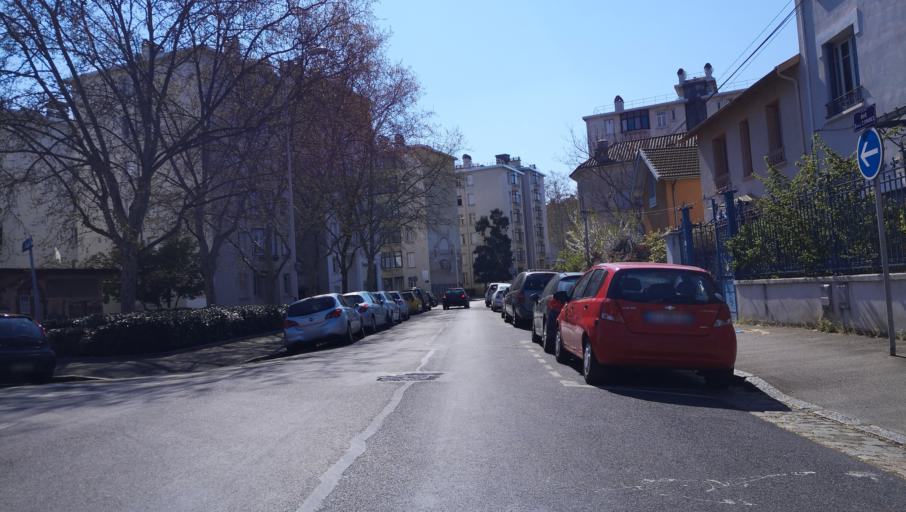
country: FR
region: Rhone-Alpes
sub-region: Departement du Rhone
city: Lyon
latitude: 45.7336
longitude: 4.8667
